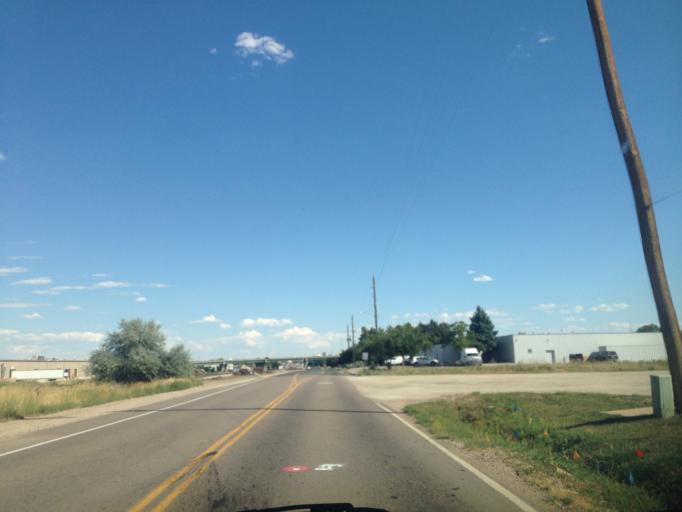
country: US
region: Colorado
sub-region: Broomfield County
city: Broomfield
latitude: 39.9209
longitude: -105.0966
